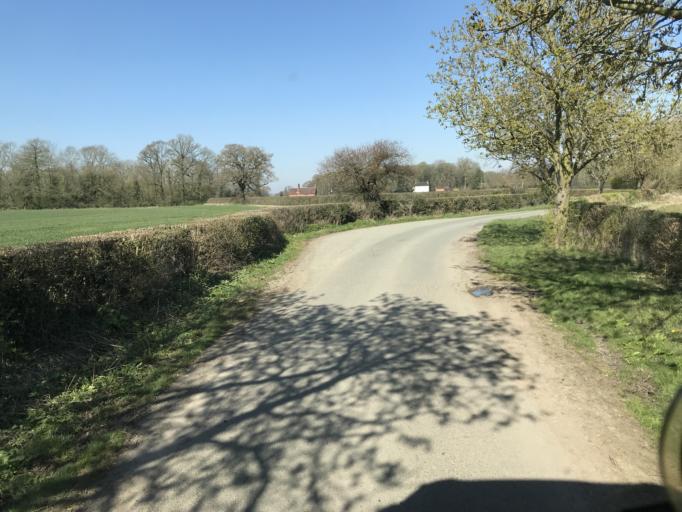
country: GB
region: England
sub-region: Cheshire West and Chester
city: Aldford
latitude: 53.1278
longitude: -2.8582
